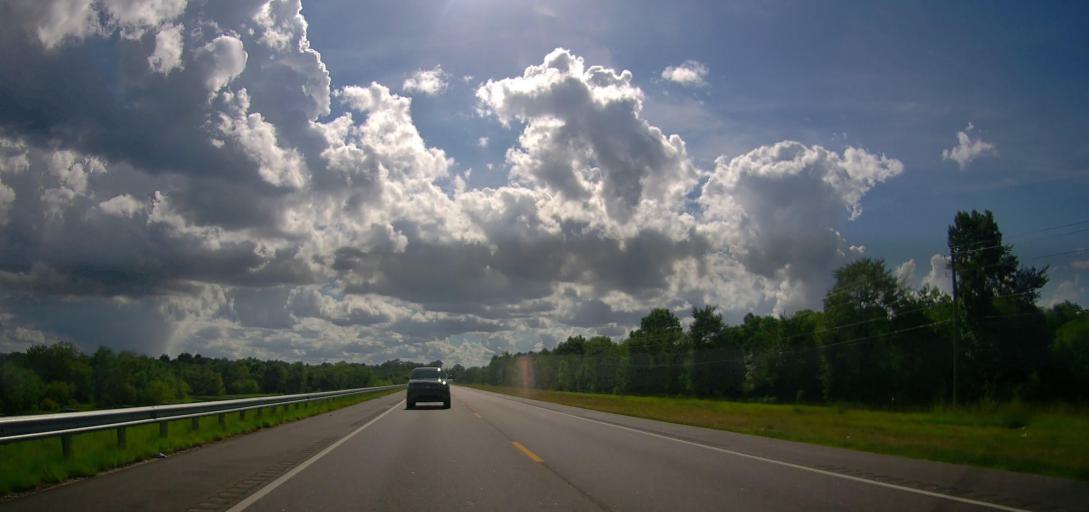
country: US
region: Alabama
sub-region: Russell County
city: Ladonia
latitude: 32.4615
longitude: -85.1337
